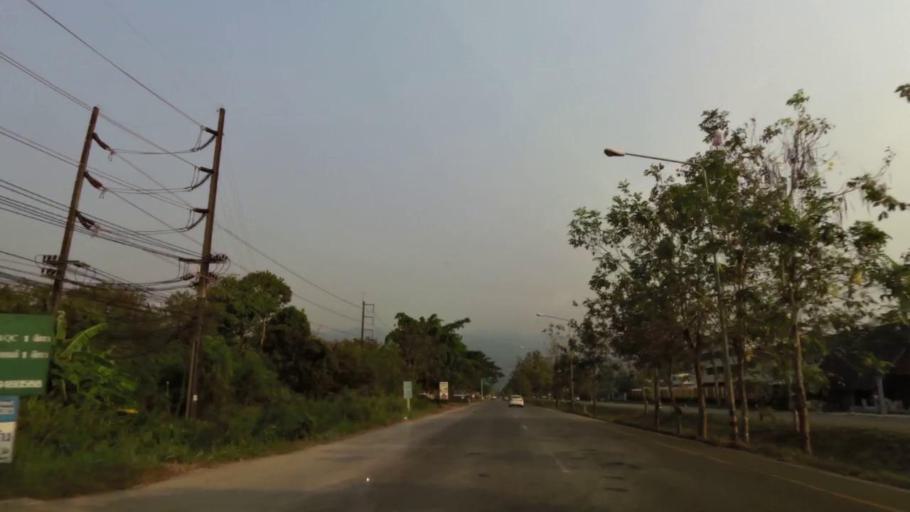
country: TH
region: Chanthaburi
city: Chanthaburi
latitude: 12.5951
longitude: 102.1447
